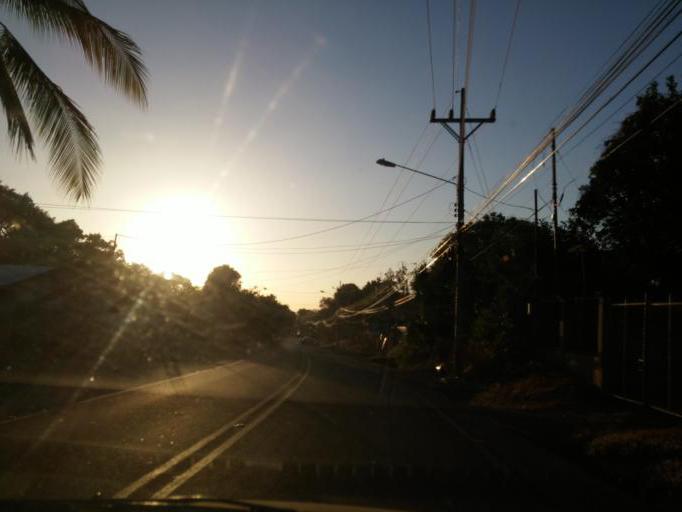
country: CR
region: Alajuela
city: Orotina
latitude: 9.9150
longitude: -84.5340
